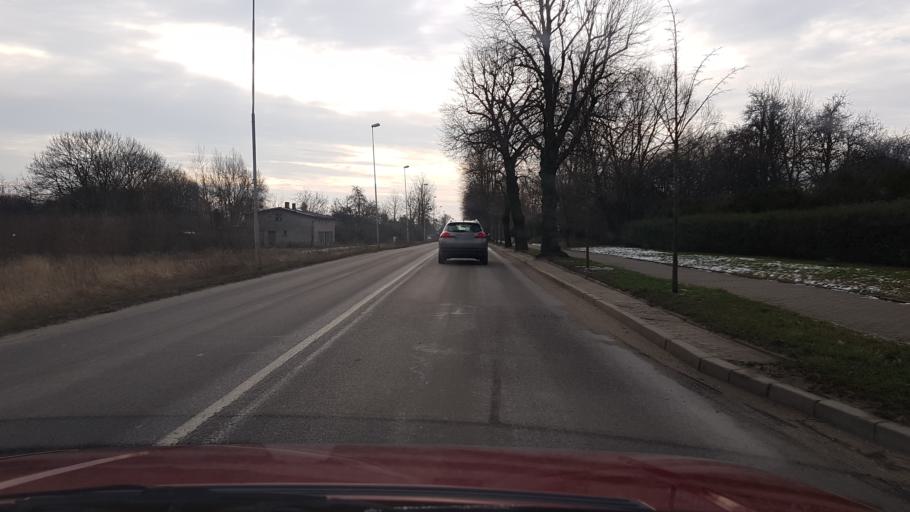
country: PL
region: West Pomeranian Voivodeship
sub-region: Szczecin
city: Szczecin
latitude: 53.4861
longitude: 14.5858
